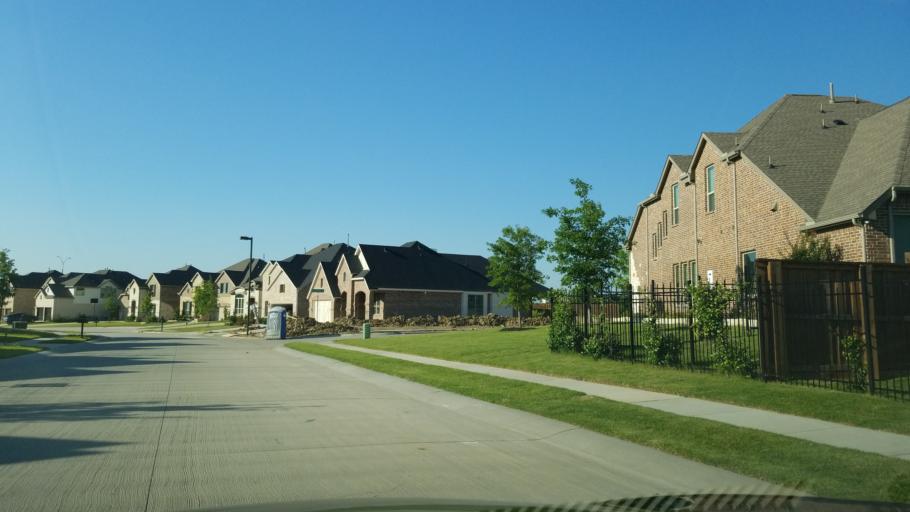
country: US
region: Texas
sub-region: Dallas County
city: Coppell
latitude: 32.9070
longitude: -96.9983
